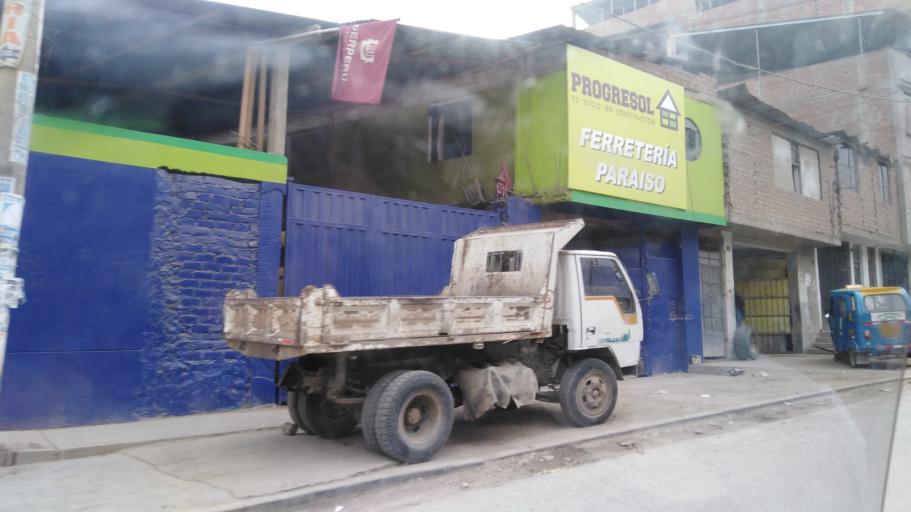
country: PE
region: Lima
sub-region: Lima
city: La Molina
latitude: -12.1464
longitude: -76.9355
